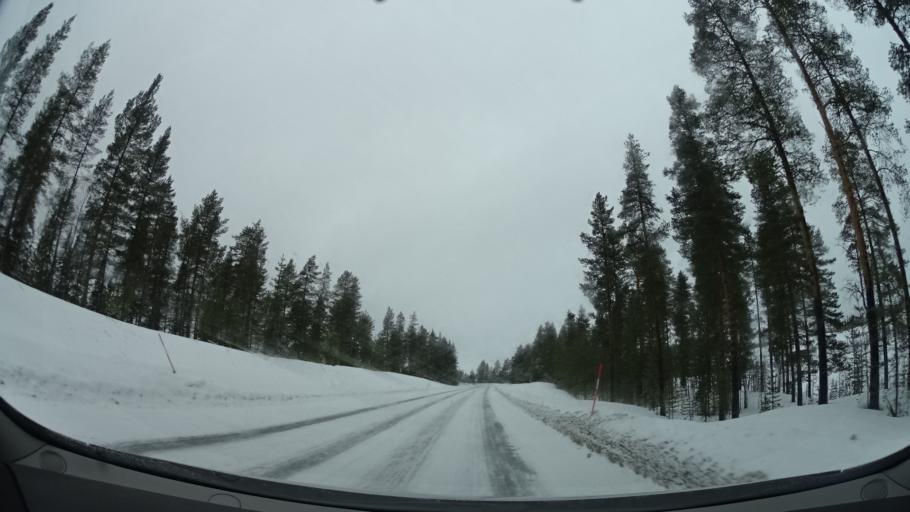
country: SE
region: Vaesterbotten
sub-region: Mala Kommun
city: Mala
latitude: 65.1430
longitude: 18.8345
